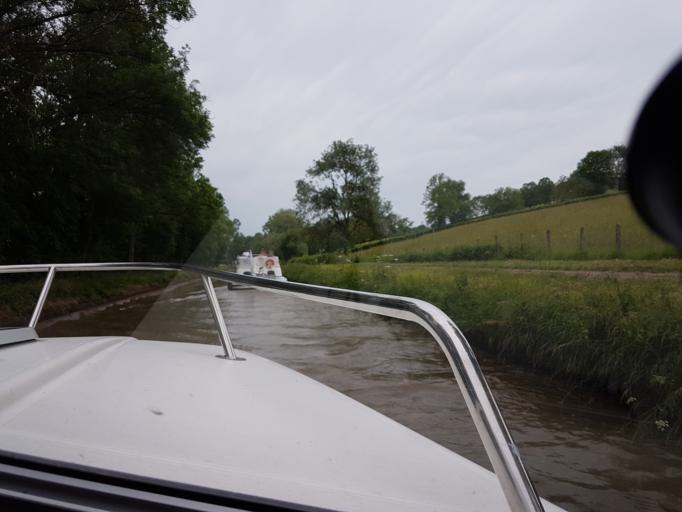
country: FR
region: Bourgogne
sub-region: Departement de la Nievre
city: Clamecy
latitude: 47.4003
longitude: 3.6044
